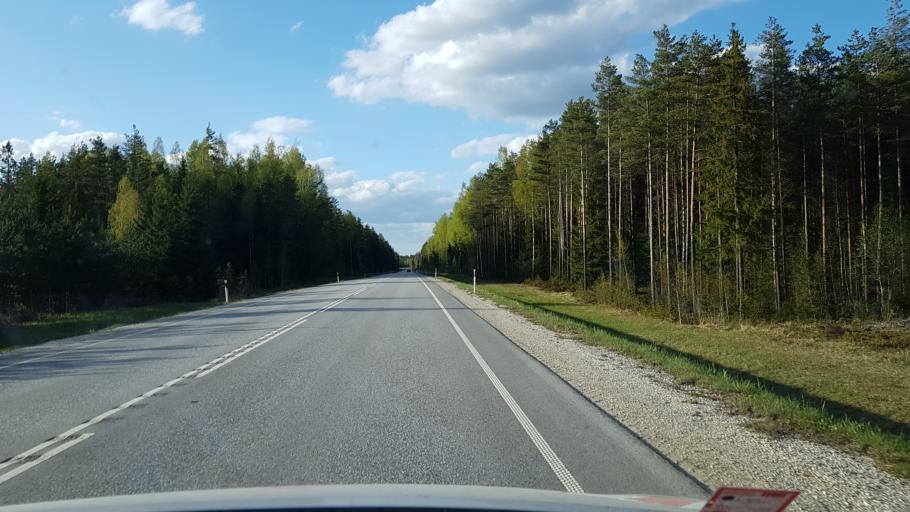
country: EE
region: Vorumaa
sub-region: Voru linn
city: Voru
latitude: 57.9504
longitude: 26.7944
